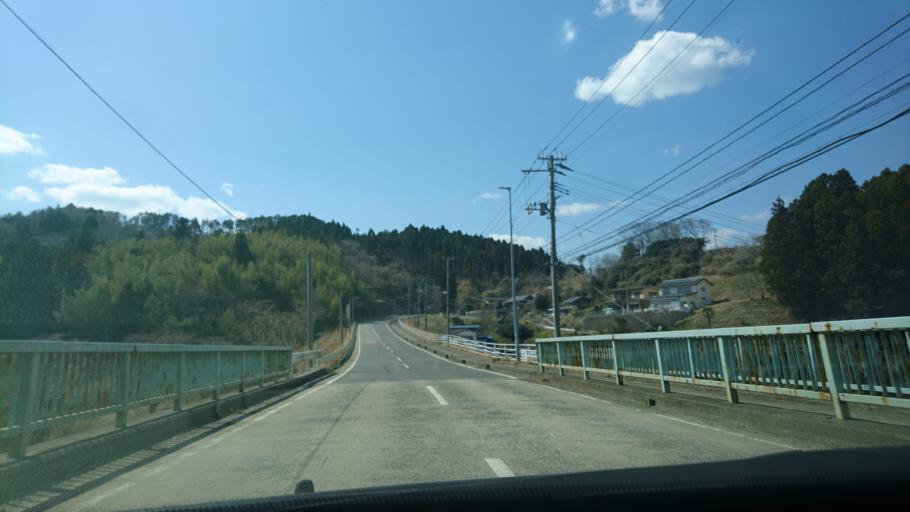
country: JP
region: Miyagi
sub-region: Oshika Gun
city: Onagawa Cho
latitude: 38.6369
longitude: 141.5018
